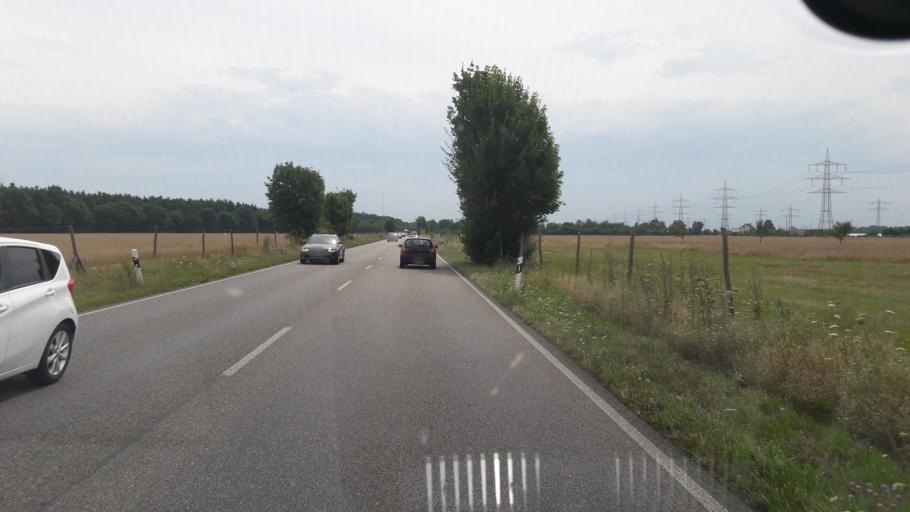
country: DE
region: Baden-Wuerttemberg
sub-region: Karlsruhe Region
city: Linkenheim-Hochstetten
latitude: 49.1247
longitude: 8.4311
